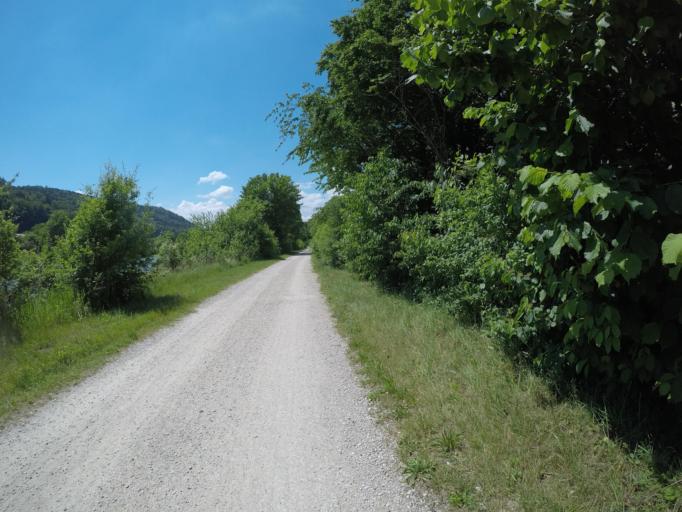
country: DE
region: Bavaria
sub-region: Lower Bavaria
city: Ihrlerstein
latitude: 48.9258
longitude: 11.8287
